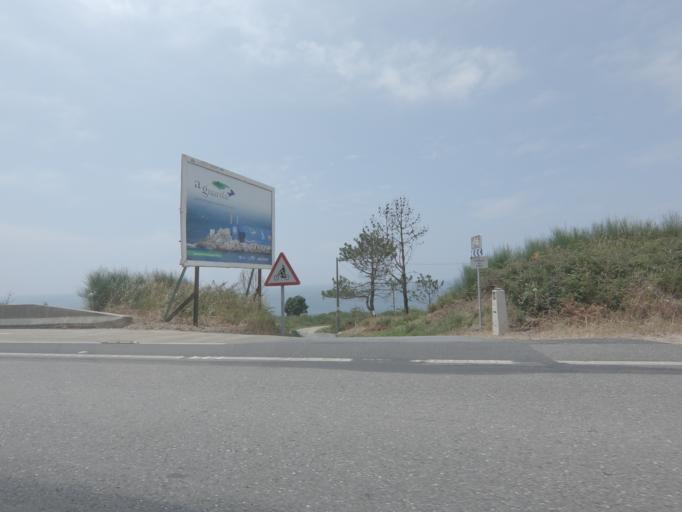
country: ES
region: Galicia
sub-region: Provincia de Pontevedra
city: A Guarda
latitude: 41.9407
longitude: -8.8840
